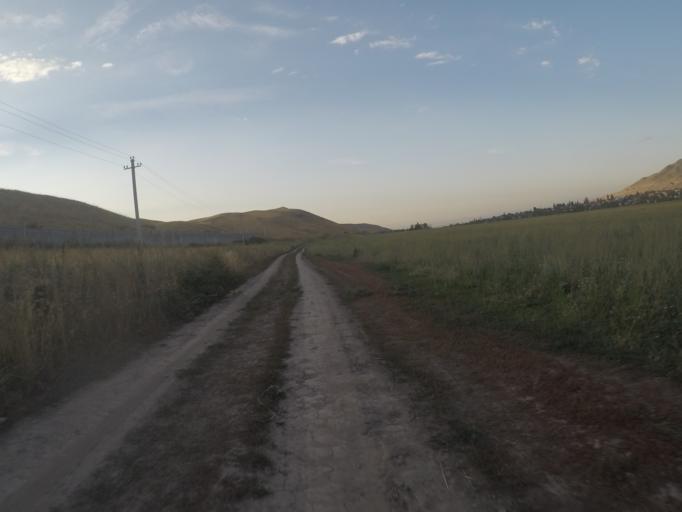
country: KG
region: Chuy
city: Bishkek
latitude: 42.7580
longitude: 74.6361
